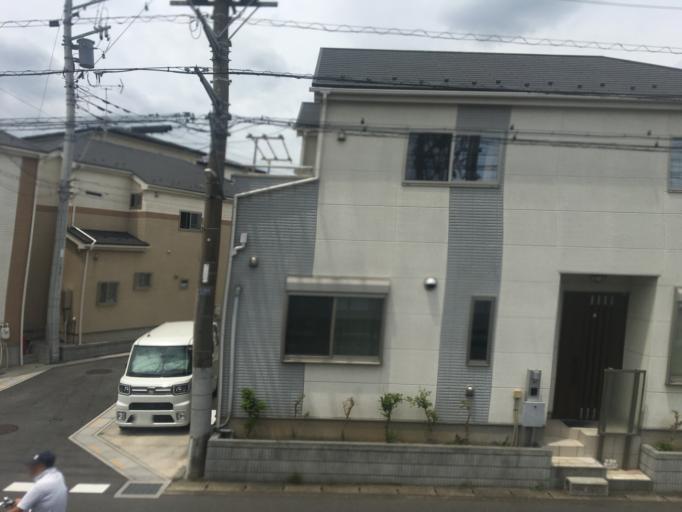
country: JP
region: Saitama
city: Koshigaya
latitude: 35.9302
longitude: 139.7761
